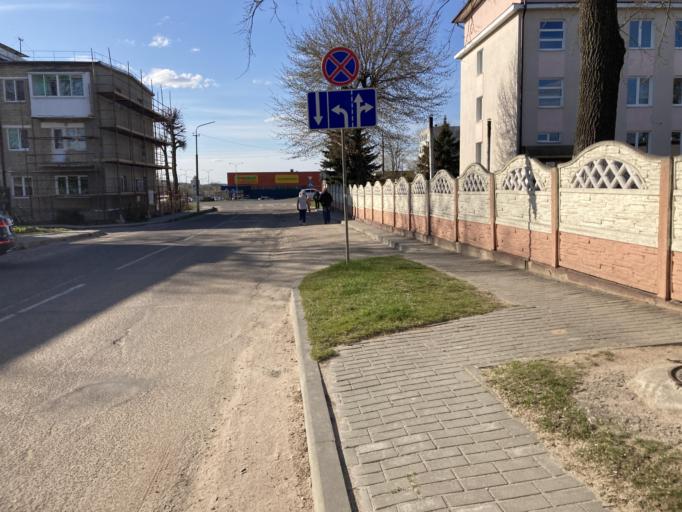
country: BY
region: Grodnenskaya
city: Slonim
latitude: 53.0859
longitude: 25.3042
